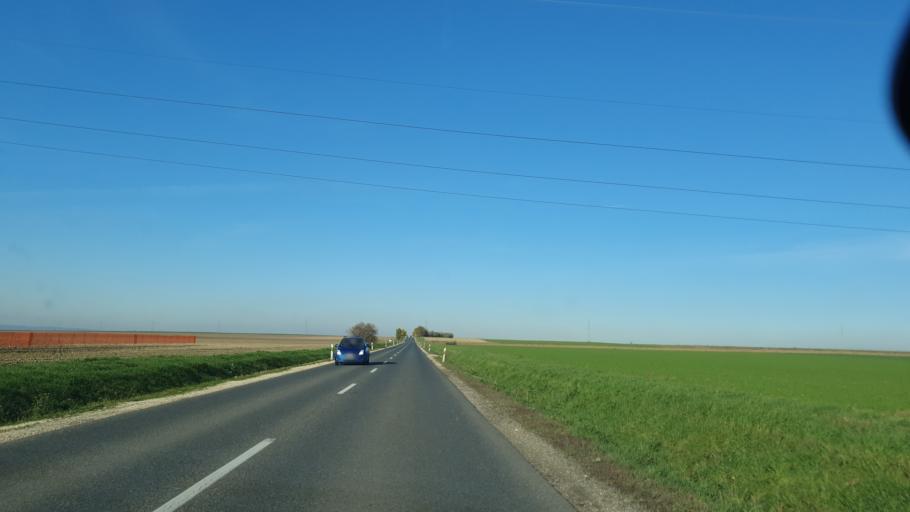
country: HU
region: Fejer
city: Szekesfehervar
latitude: 47.2266
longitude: 18.4165
